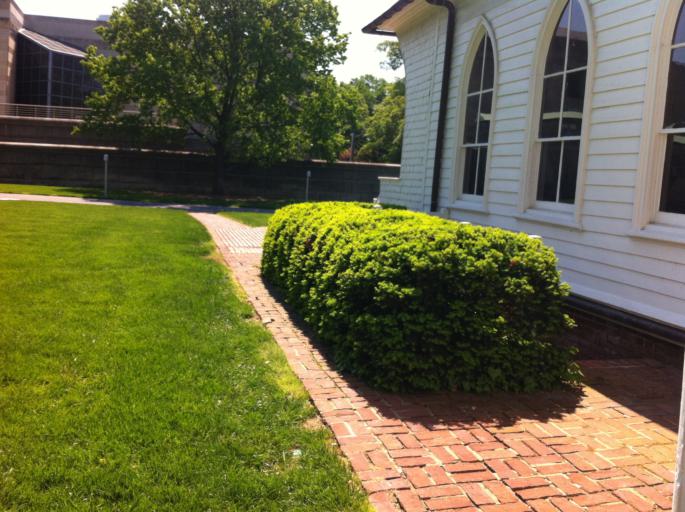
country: US
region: Virginia
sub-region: City of Richmond
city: Richmond
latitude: 37.5560
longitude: -77.4762
